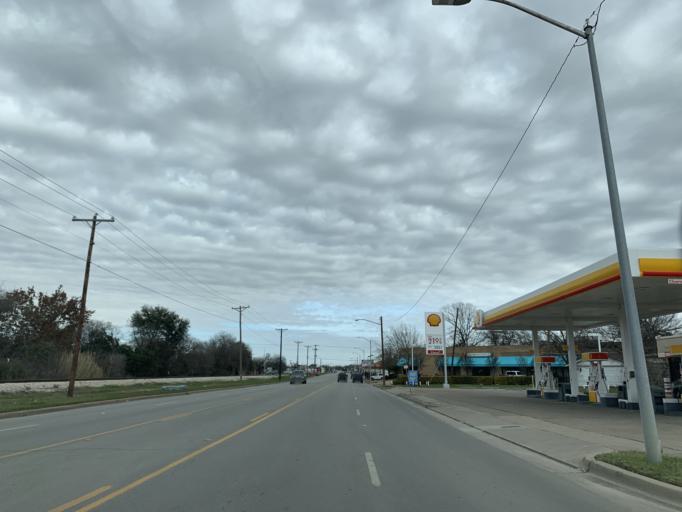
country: US
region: Texas
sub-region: Tarrant County
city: Fort Worth
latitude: 32.7026
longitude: -97.3513
